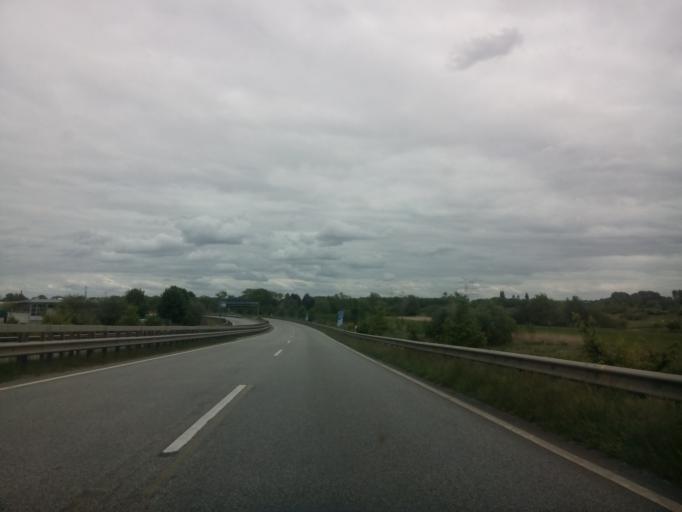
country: DE
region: Lower Saxony
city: Stuhr
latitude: 53.0760
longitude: 8.7448
